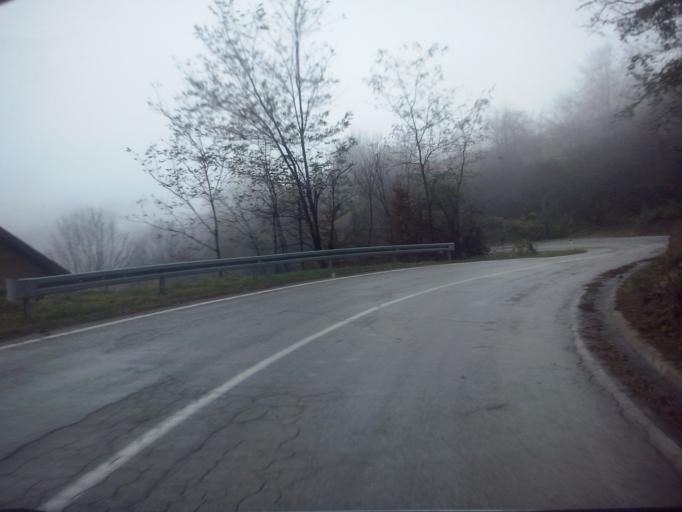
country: RS
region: Central Serbia
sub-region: Moravicki Okrug
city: Ivanjica
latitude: 43.5340
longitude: 20.2947
